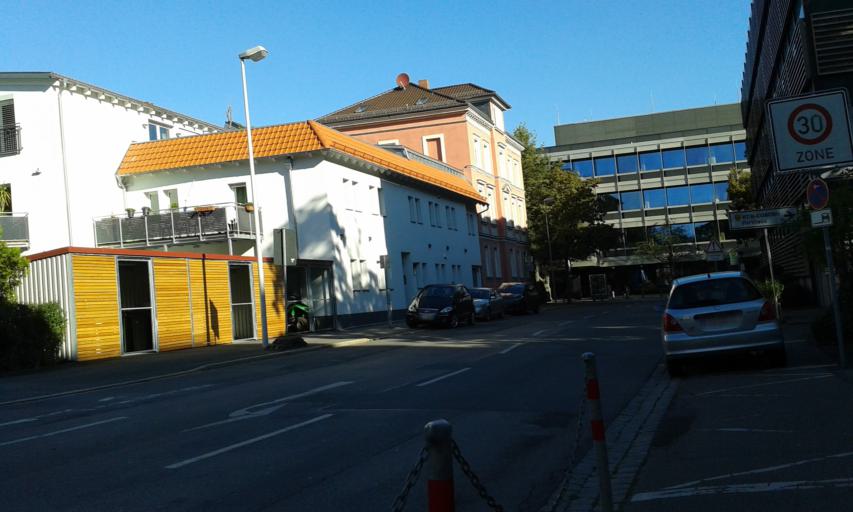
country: DE
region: Bavaria
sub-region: Upper Franconia
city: Coburg
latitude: 50.2623
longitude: 10.9600
